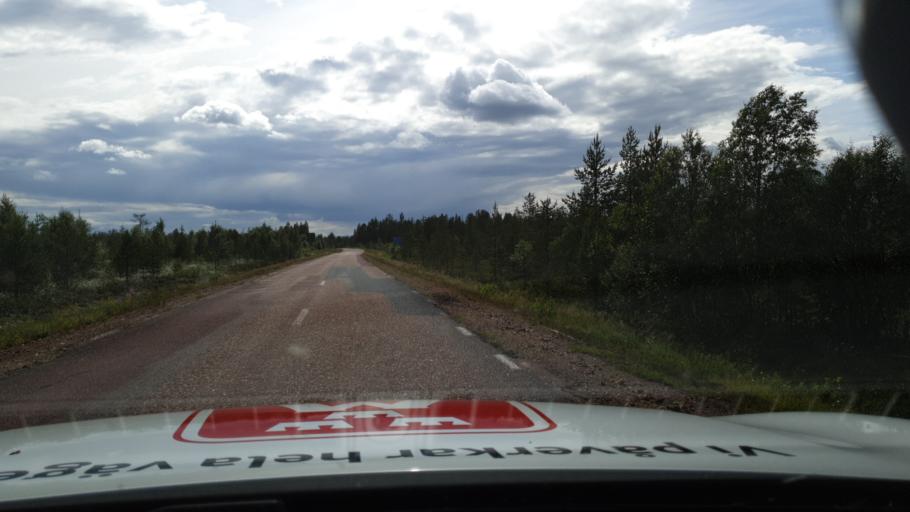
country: SE
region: Dalarna
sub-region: Alvdalens Kommun
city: AElvdalen
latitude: 61.7611
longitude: 13.4623
